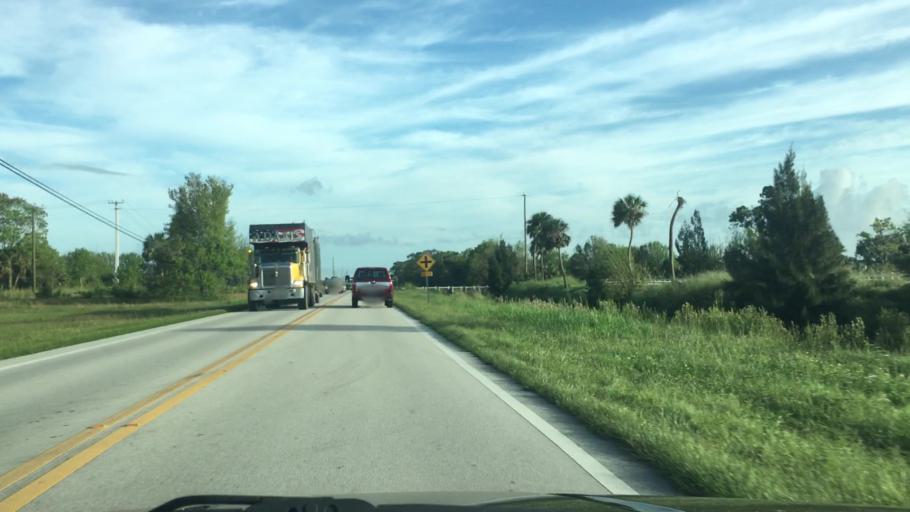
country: US
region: Florida
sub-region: Indian River County
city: Winter Beach
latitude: 27.6886
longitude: -80.4627
